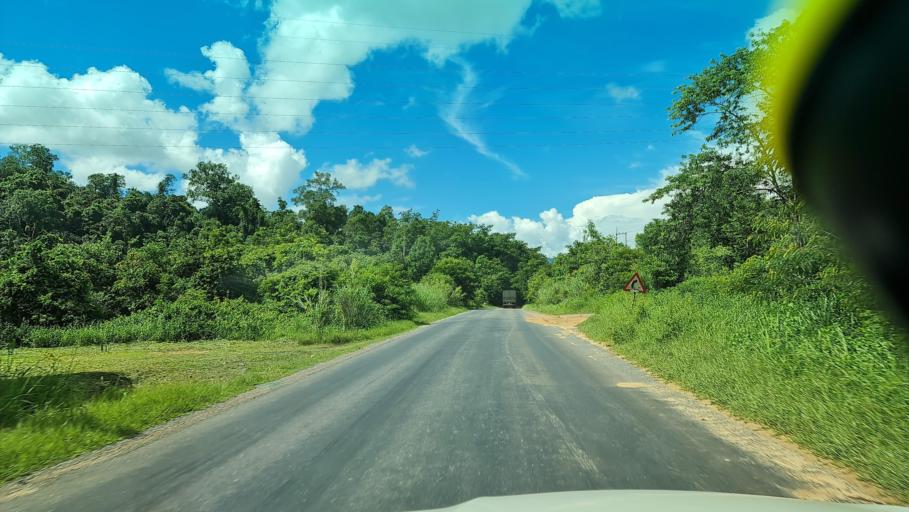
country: LA
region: Bolikhamxai
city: Pakkading
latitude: 18.2866
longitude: 104.0745
